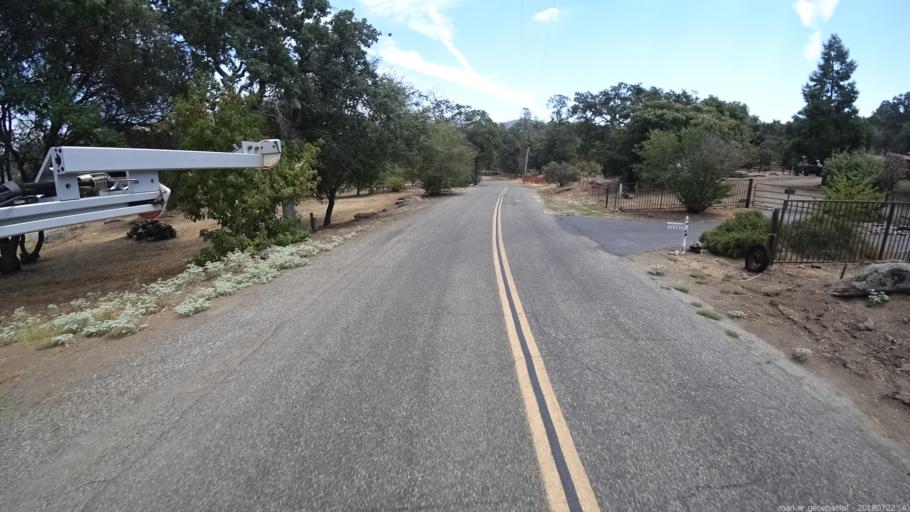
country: US
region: California
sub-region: Madera County
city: Coarsegold
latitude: 37.2825
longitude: -119.7416
